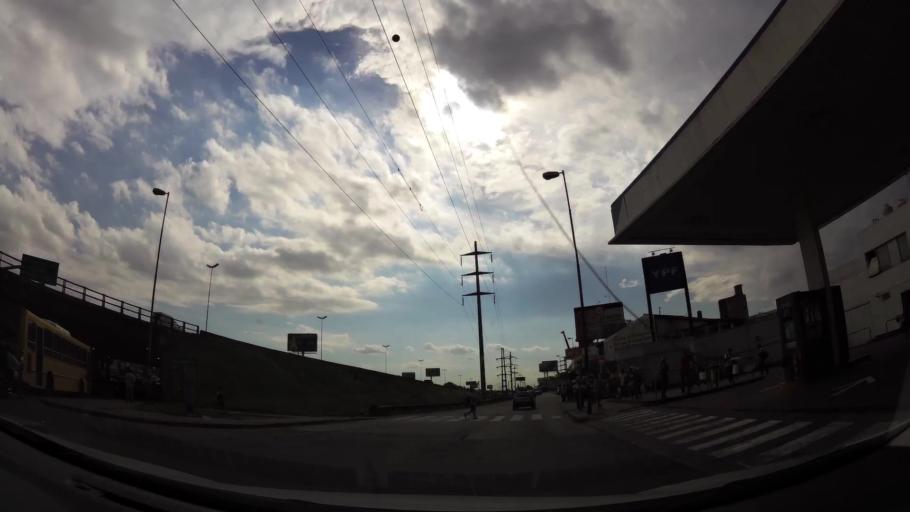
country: AR
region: Buenos Aires
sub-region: Partido de Tigre
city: Tigre
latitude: -34.4850
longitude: -58.6144
